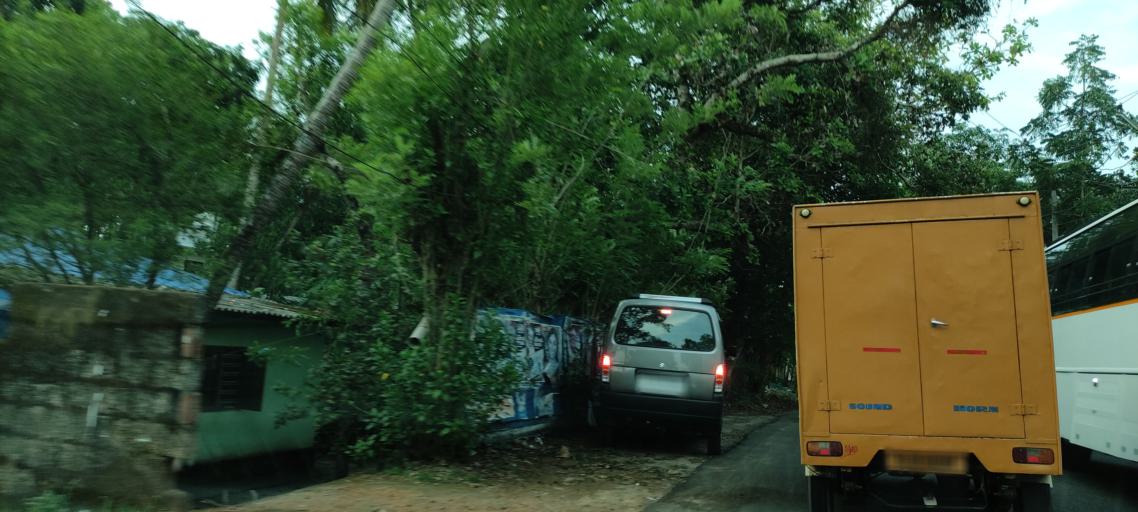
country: IN
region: Kerala
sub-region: Kottayam
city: Vaikam
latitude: 9.7712
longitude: 76.3625
